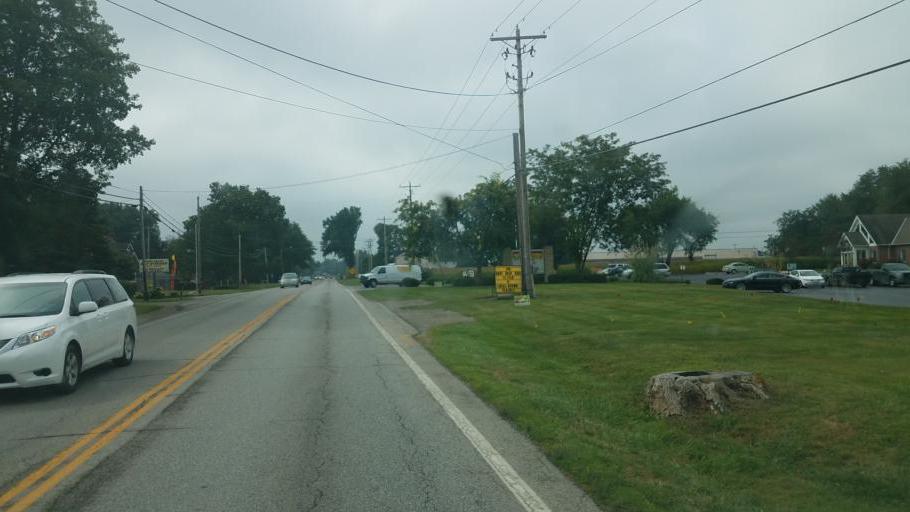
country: US
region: Ohio
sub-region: Knox County
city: Mount Vernon
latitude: 40.3688
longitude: -82.4809
